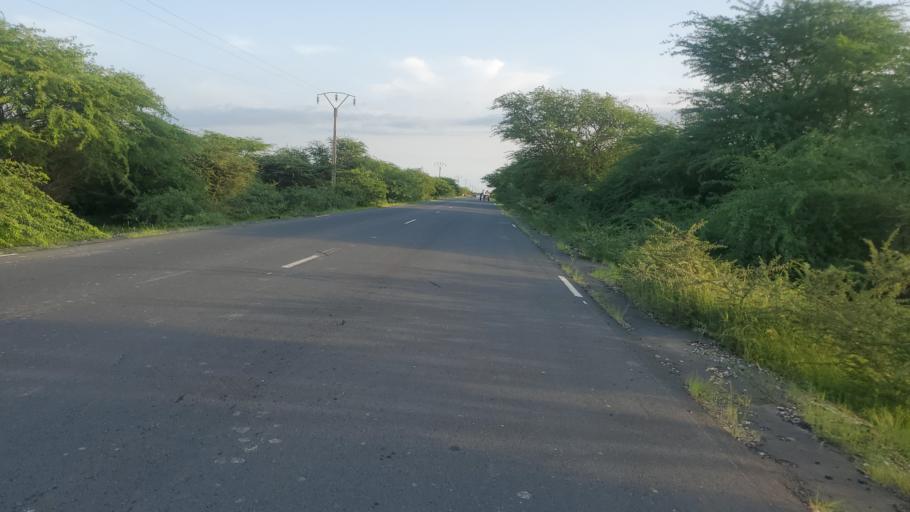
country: SN
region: Saint-Louis
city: Saint-Louis
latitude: 16.1900
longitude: -16.4093
